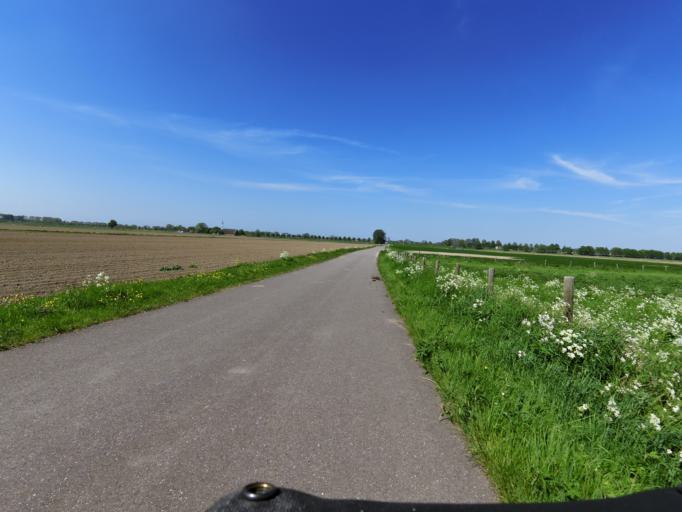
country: NL
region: South Holland
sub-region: Gemeente Binnenmaas
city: Heinenoord
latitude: 51.8364
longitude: 4.4682
